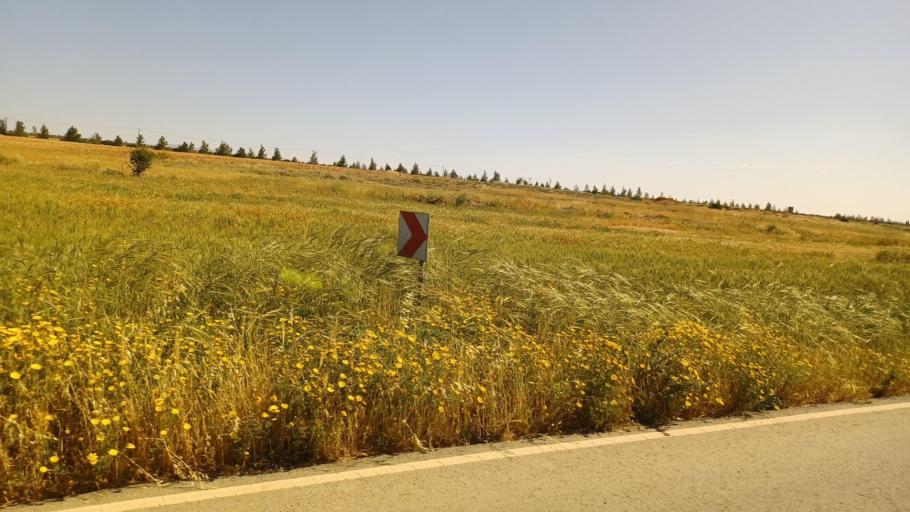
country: CY
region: Lefkosia
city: Kokkinotrimithia
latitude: 35.1582
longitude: 33.1793
